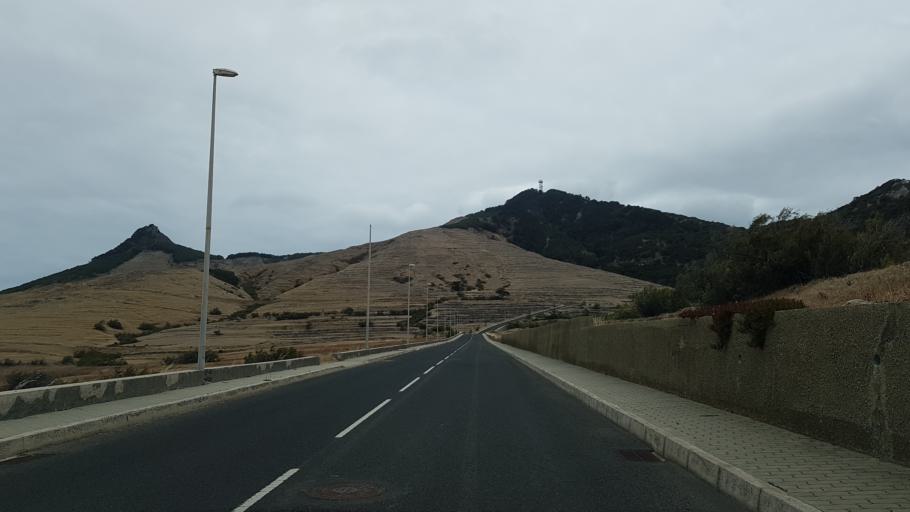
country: PT
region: Madeira
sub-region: Porto Santo
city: Camacha
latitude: 33.0895
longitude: -16.3403
